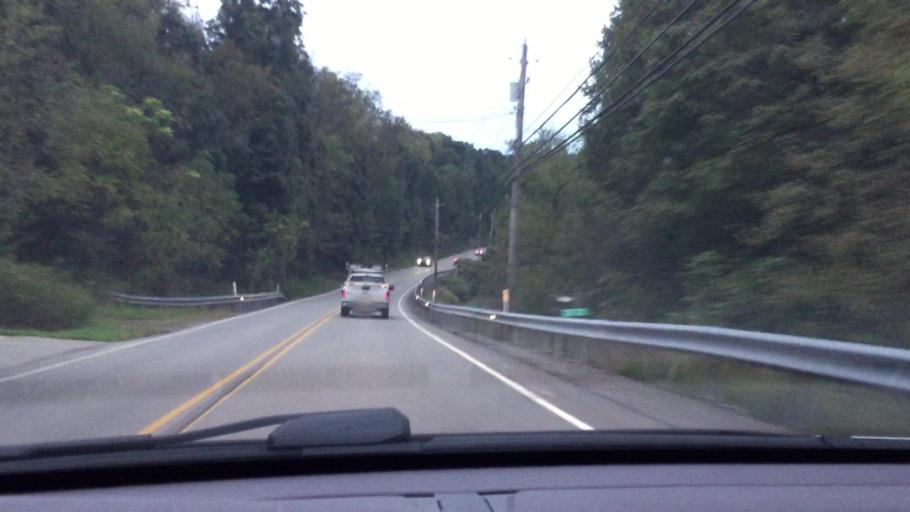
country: US
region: Pennsylvania
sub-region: Westmoreland County
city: West Newton
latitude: 40.1959
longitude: -79.7930
